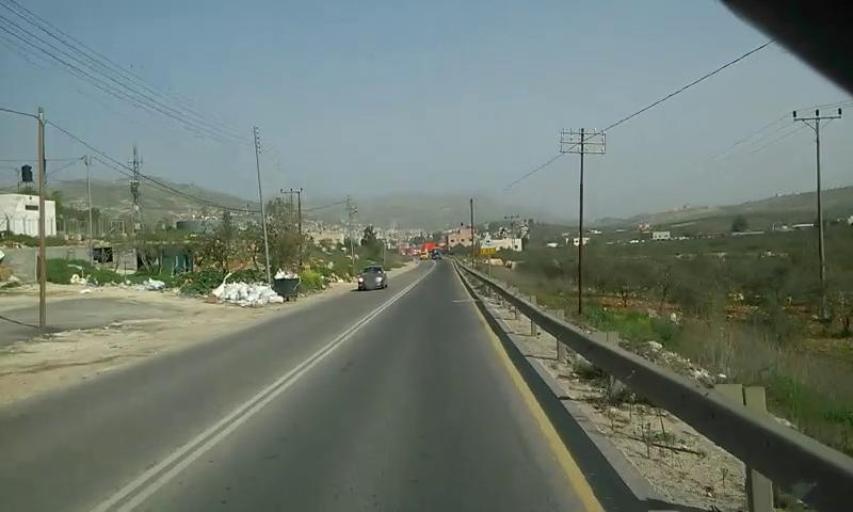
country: PS
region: West Bank
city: `Aynabus
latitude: 32.1336
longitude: 35.2579
